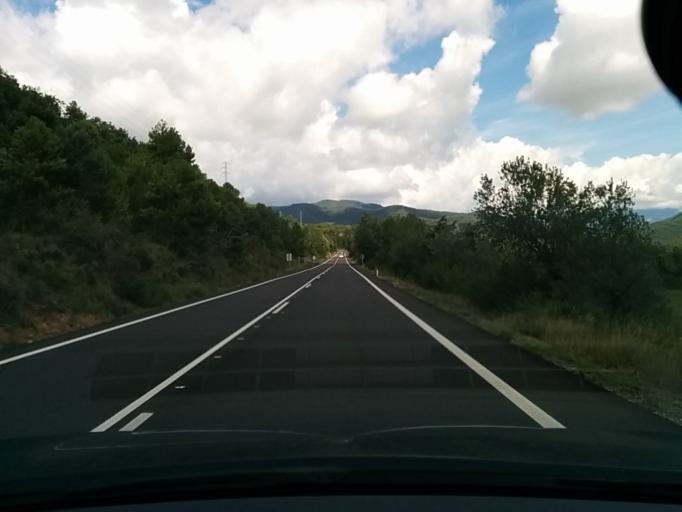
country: ES
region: Aragon
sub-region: Provincia de Huesca
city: Labuerda
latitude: 42.4360
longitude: 0.1309
